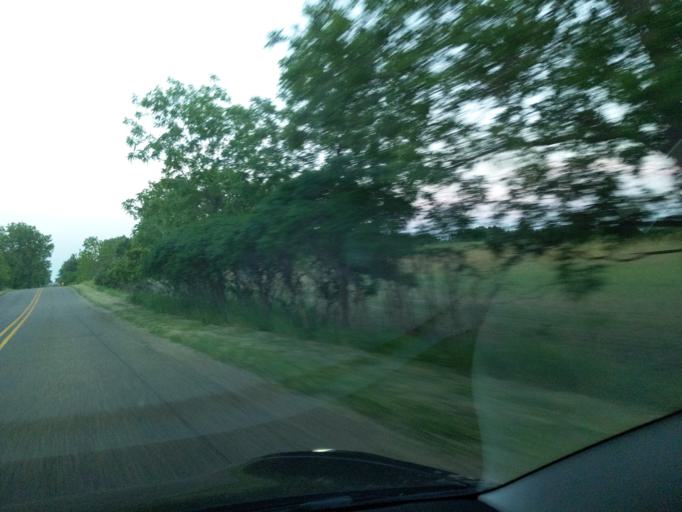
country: US
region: Michigan
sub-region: Eaton County
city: Bellevue
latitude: 42.5387
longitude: -84.9704
